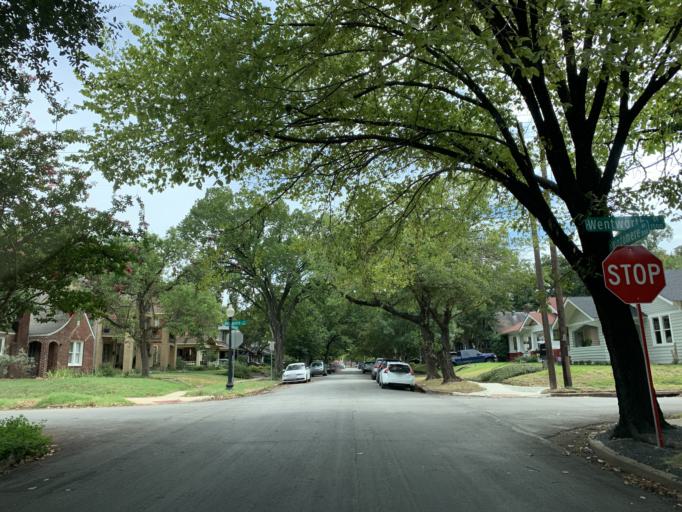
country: US
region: Texas
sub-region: Dallas County
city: Cockrell Hill
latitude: 32.7433
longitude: -96.8454
